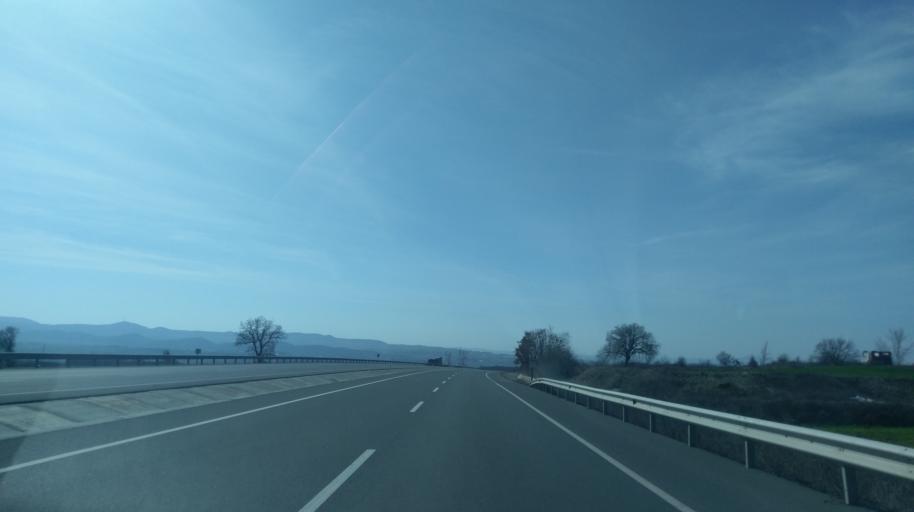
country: TR
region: Edirne
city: Kesan
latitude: 40.9133
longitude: 26.6345
